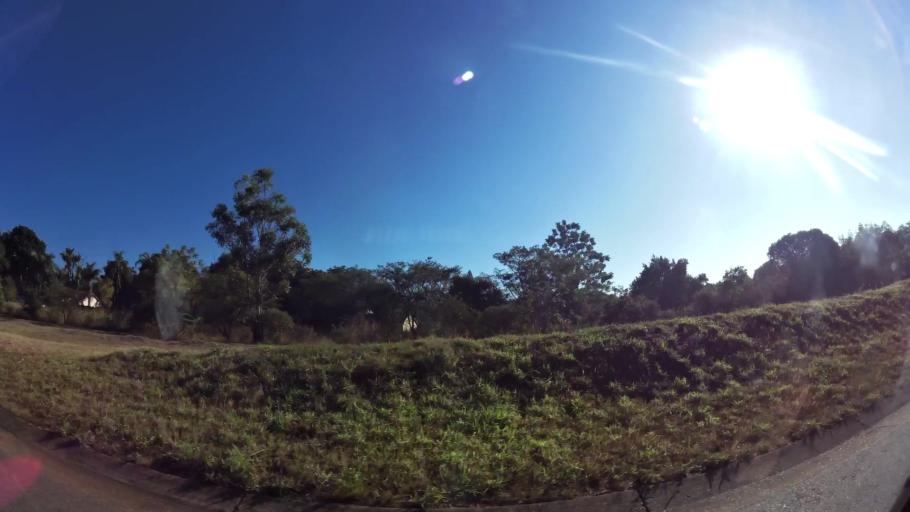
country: ZA
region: Limpopo
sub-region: Mopani District Municipality
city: Tzaneen
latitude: -23.8302
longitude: 30.1478
